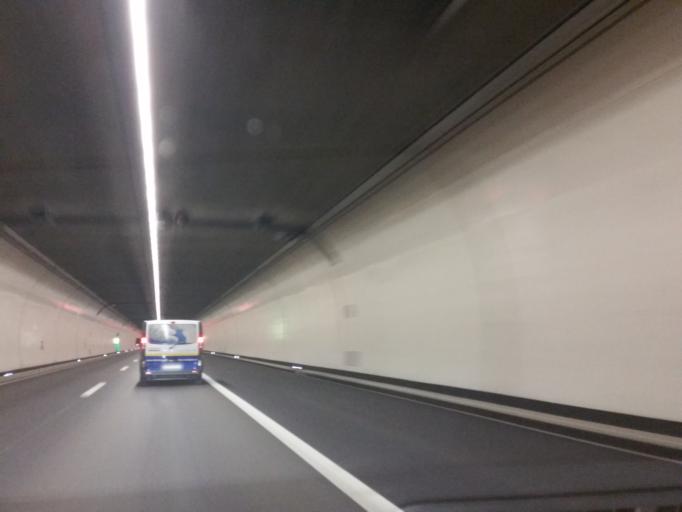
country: CH
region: Zurich
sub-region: Bezirk Zuerich
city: Zuerich (Kreis 2)
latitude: 47.3444
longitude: 8.5143
